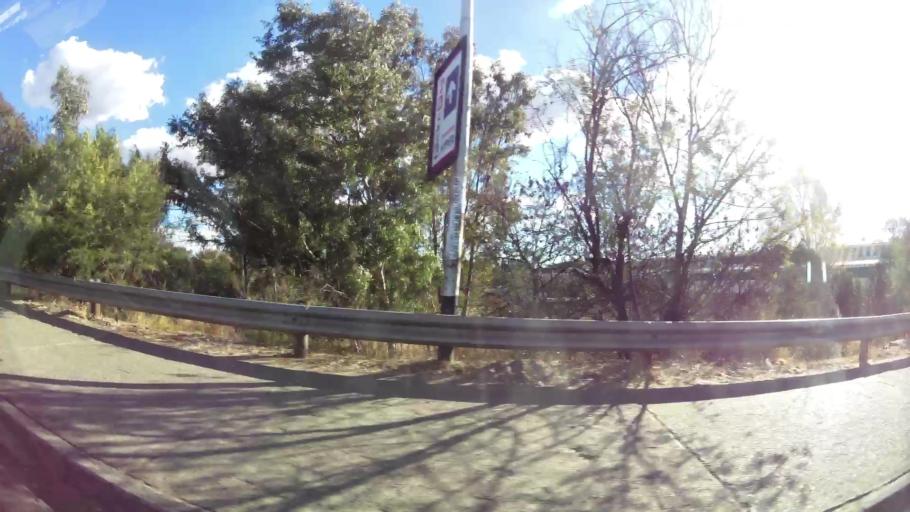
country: ZA
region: North-West
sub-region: Dr Kenneth Kaunda District Municipality
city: Klerksdorp
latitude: -26.8596
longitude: 26.6651
